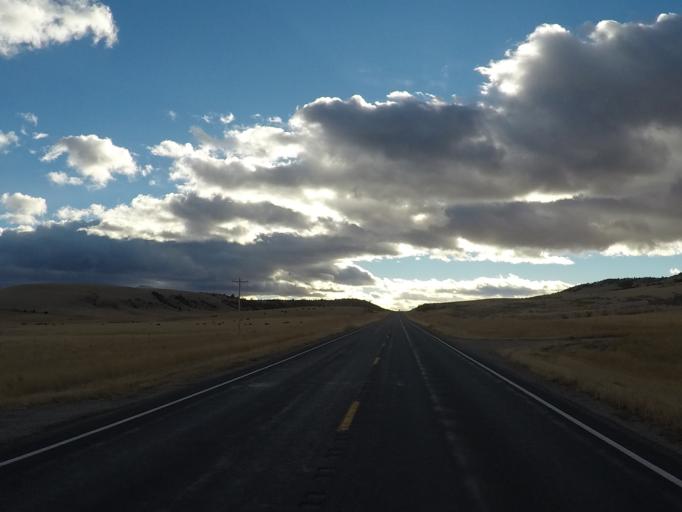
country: US
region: Montana
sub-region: Jefferson County
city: Whitehall
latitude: 45.9142
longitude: -111.9353
